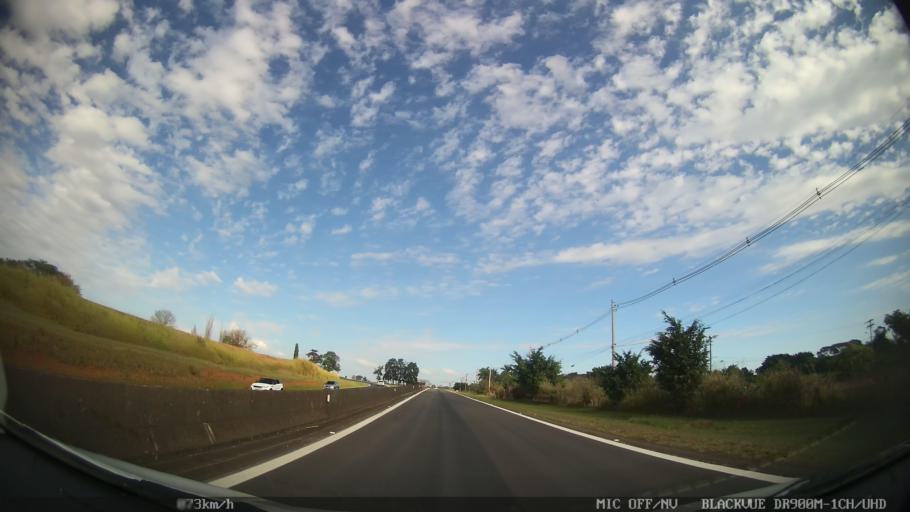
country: BR
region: Sao Paulo
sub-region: Iracemapolis
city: Iracemapolis
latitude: -22.5862
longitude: -47.4598
